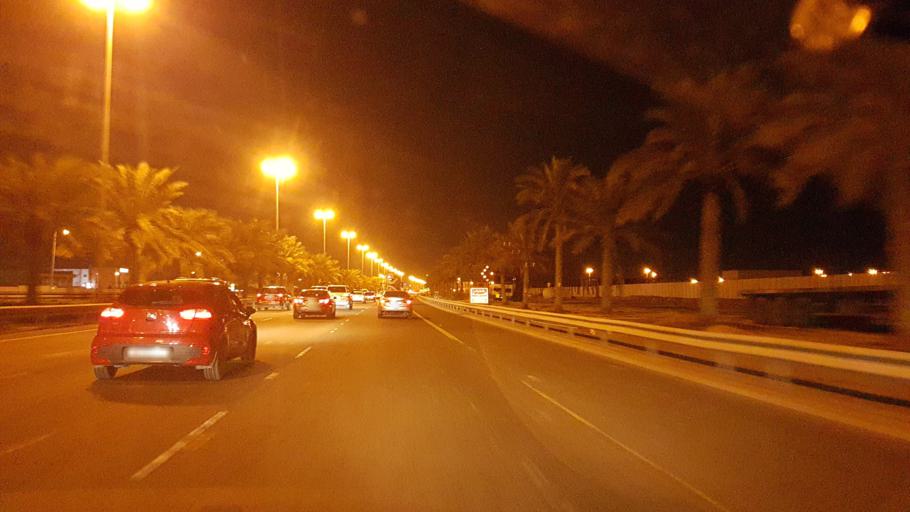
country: BH
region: Muharraq
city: Al Hadd
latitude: 26.2386
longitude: 50.6579
